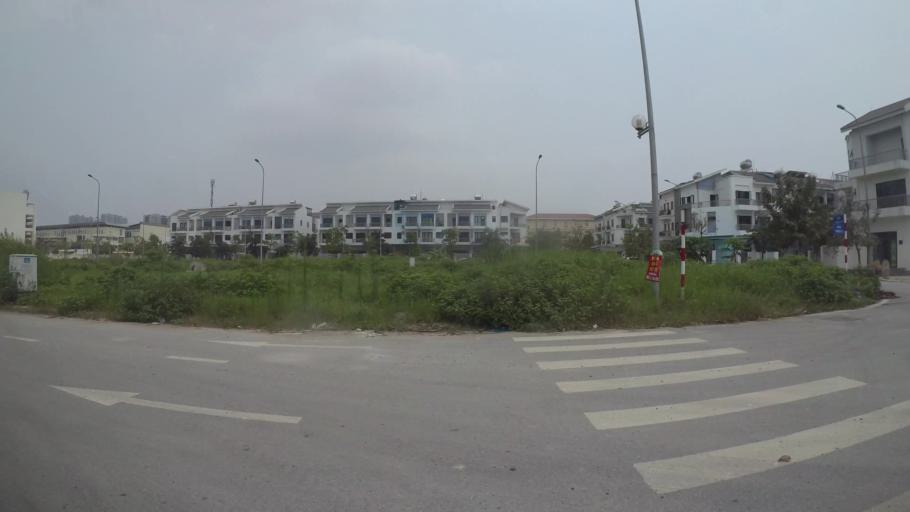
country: VN
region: Ha Noi
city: Cau Dien
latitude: 21.0312
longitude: 105.7463
